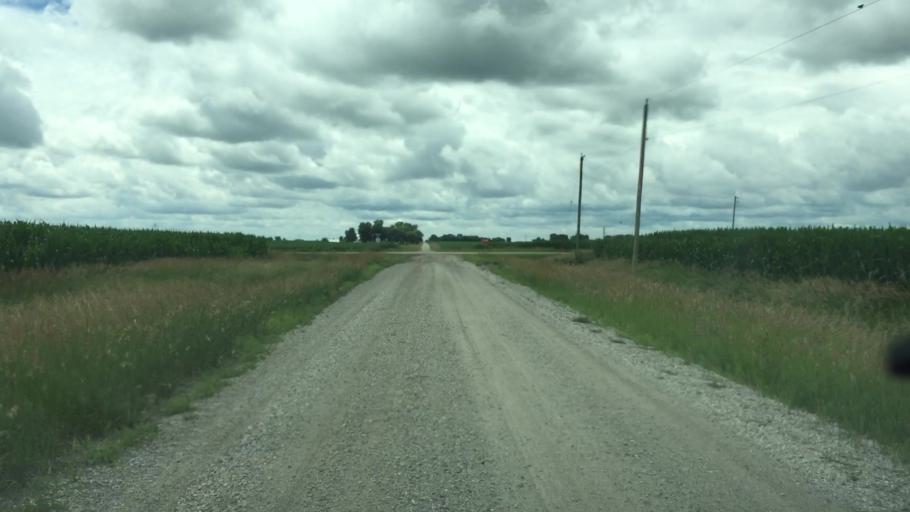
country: US
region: Iowa
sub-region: Jasper County
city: Prairie City
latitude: 41.5817
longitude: -93.1596
